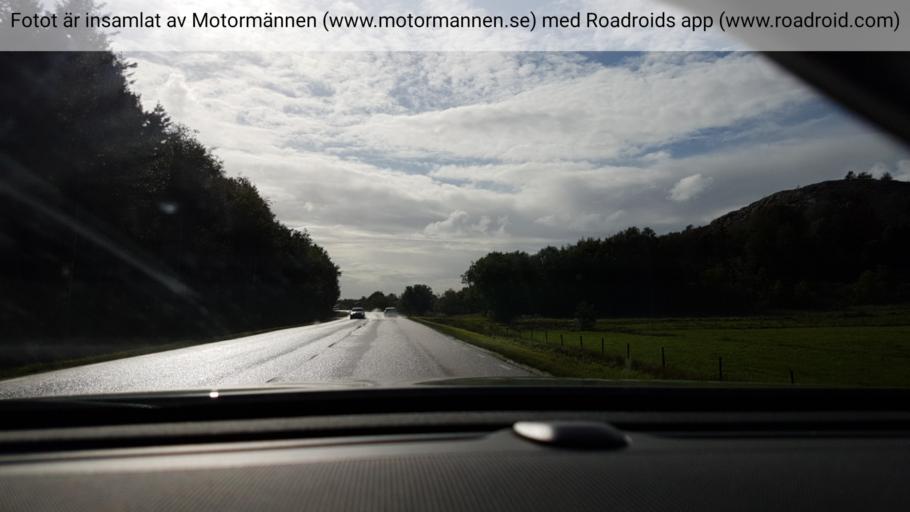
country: SE
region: Vaestra Goetaland
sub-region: Tjorns Kommun
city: Skaerhamn
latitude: 57.9921
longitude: 11.5817
